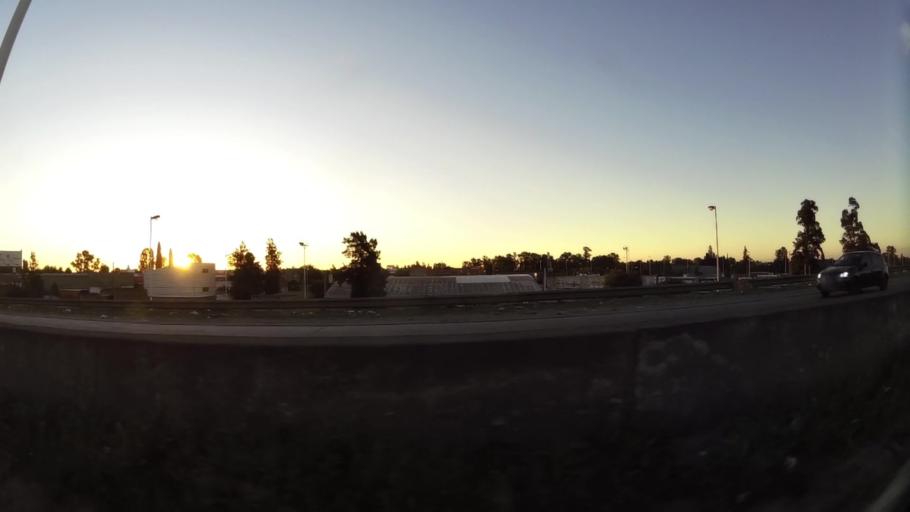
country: AR
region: Buenos Aires
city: Pontevedra
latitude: -34.7615
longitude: -58.6162
